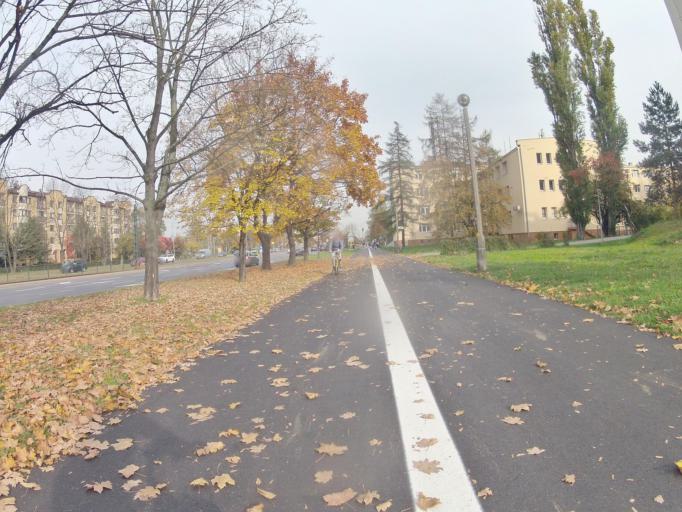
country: PL
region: Lesser Poland Voivodeship
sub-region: Krakow
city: Krakow
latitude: 50.0456
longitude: 19.9227
